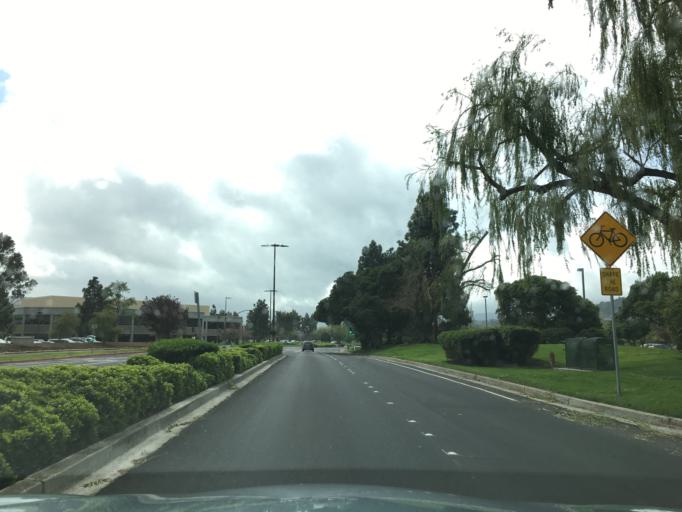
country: US
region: California
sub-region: San Mateo County
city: Belmont
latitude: 37.5275
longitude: -122.2638
